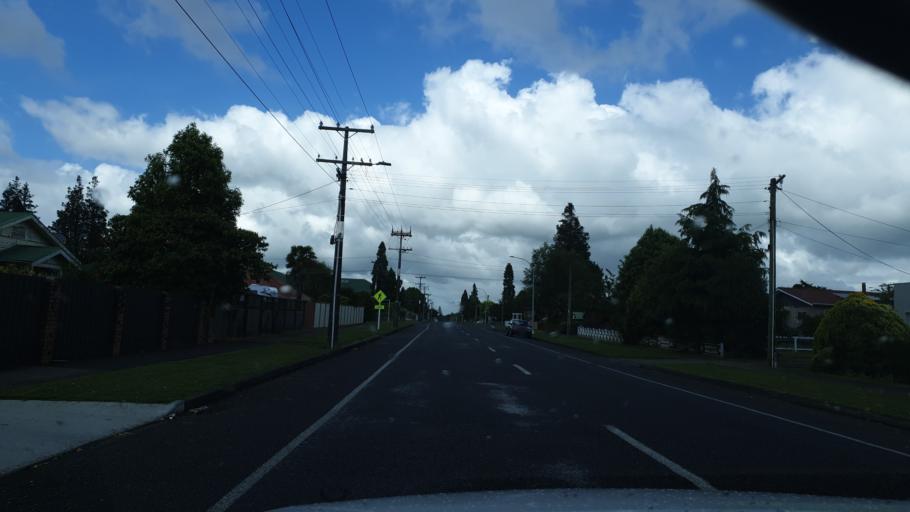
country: NZ
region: Waikato
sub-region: Matamata-Piako District
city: Matamata
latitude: -37.8102
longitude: 175.7675
